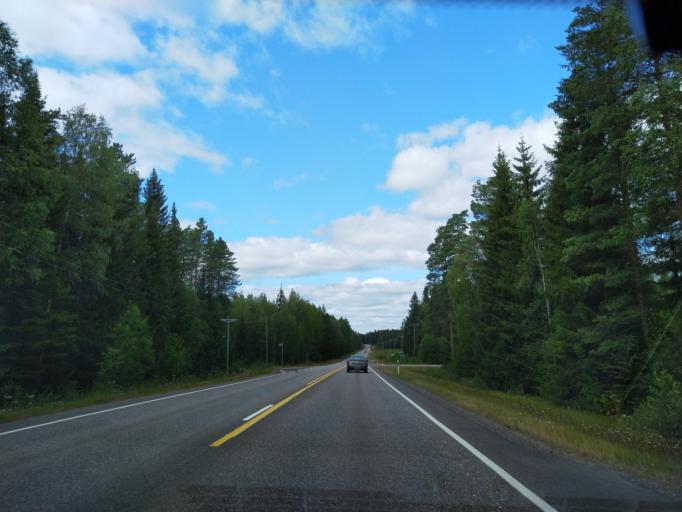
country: FI
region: Haeme
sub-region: Haemeenlinna
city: Renko
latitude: 60.7532
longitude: 24.3060
